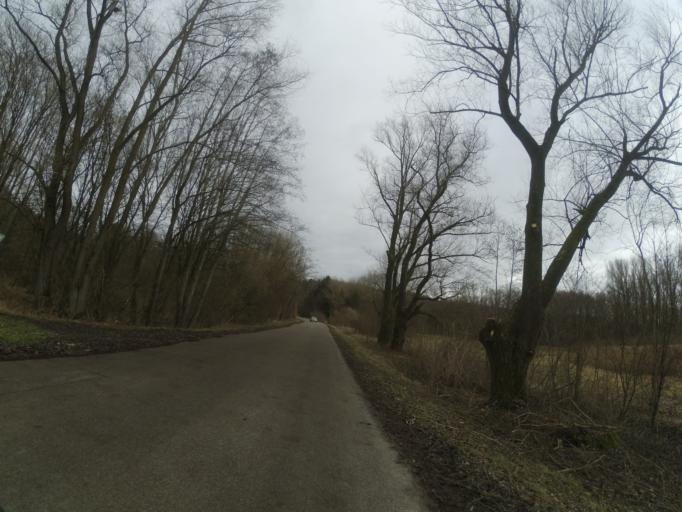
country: DE
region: Bavaria
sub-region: Swabia
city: Vohringen
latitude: 48.2975
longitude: 10.0913
